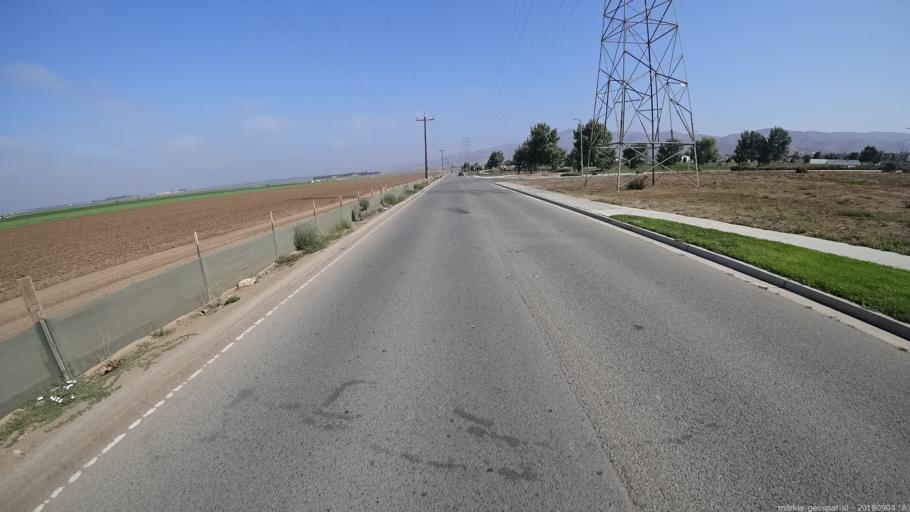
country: US
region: California
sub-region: Monterey County
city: Soledad
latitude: 36.4359
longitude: -121.3336
